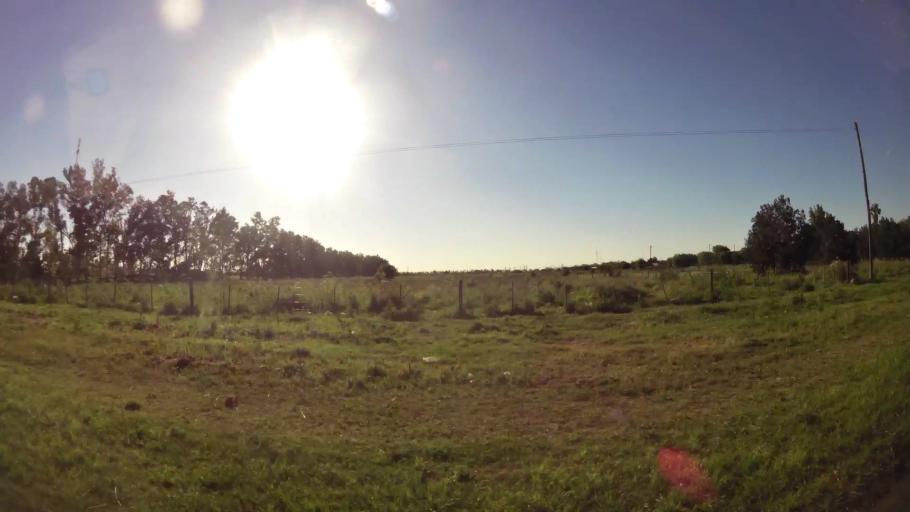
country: AR
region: Cordoba
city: San Francisco
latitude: -31.4447
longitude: -62.0996
